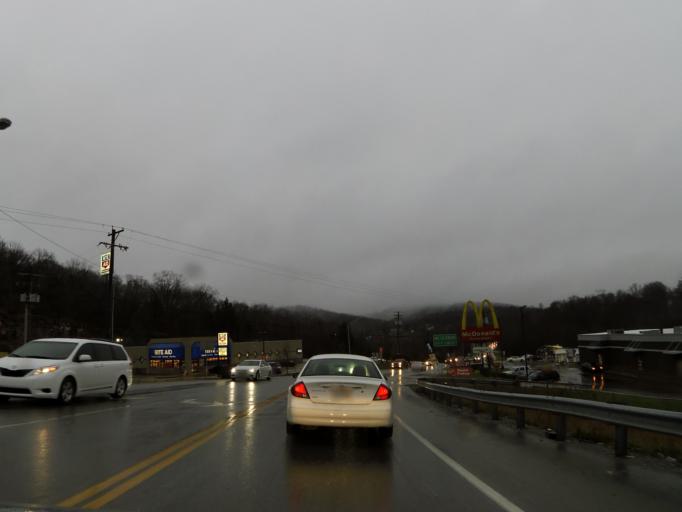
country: US
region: Kentucky
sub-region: Rockcastle County
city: Mount Vernon
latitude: 37.3680
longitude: -84.3370
